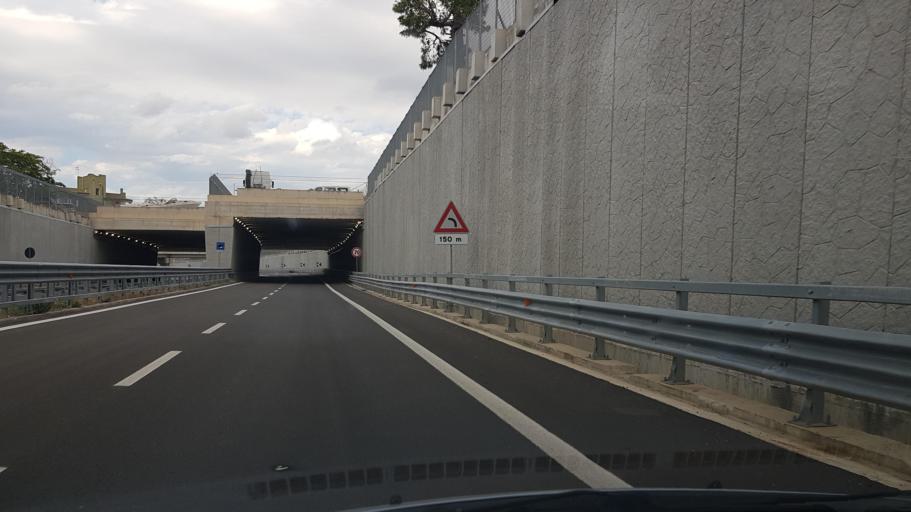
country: IT
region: Apulia
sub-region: Provincia di Taranto
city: Taranto
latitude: 40.4604
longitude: 17.2877
